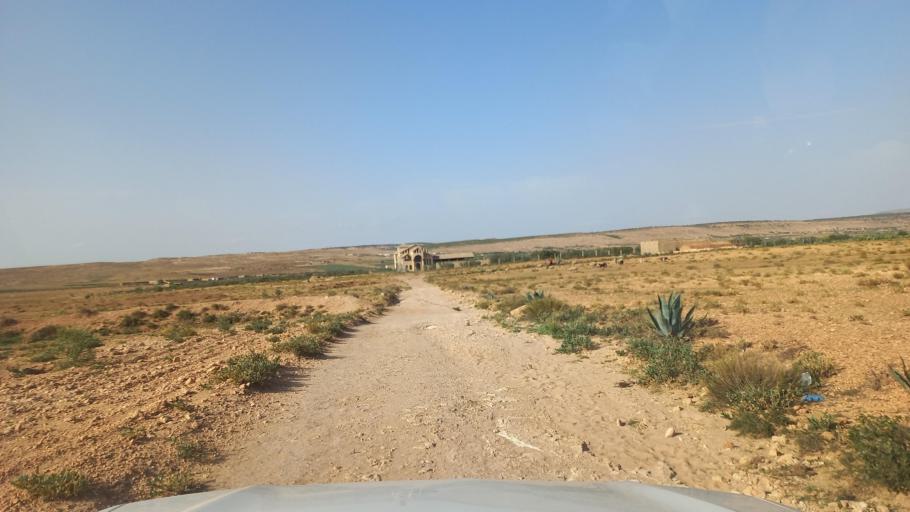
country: TN
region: Al Qasrayn
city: Kasserine
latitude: 35.3410
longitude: 8.8454
